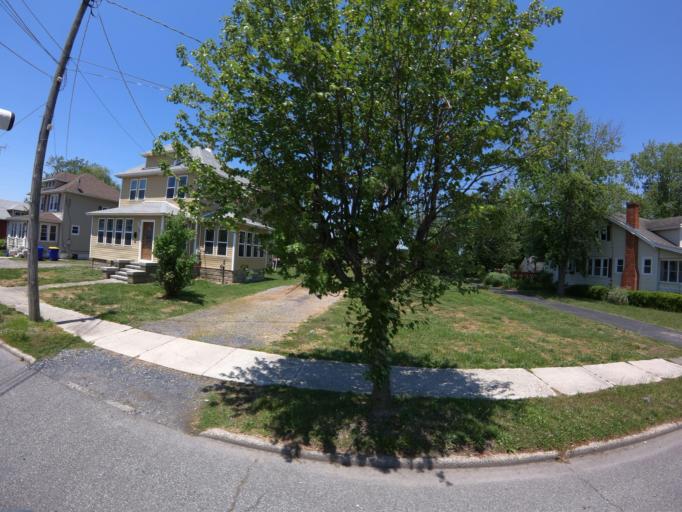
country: US
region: Delaware
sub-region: Kent County
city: Harrington
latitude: 38.9232
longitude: -75.5741
